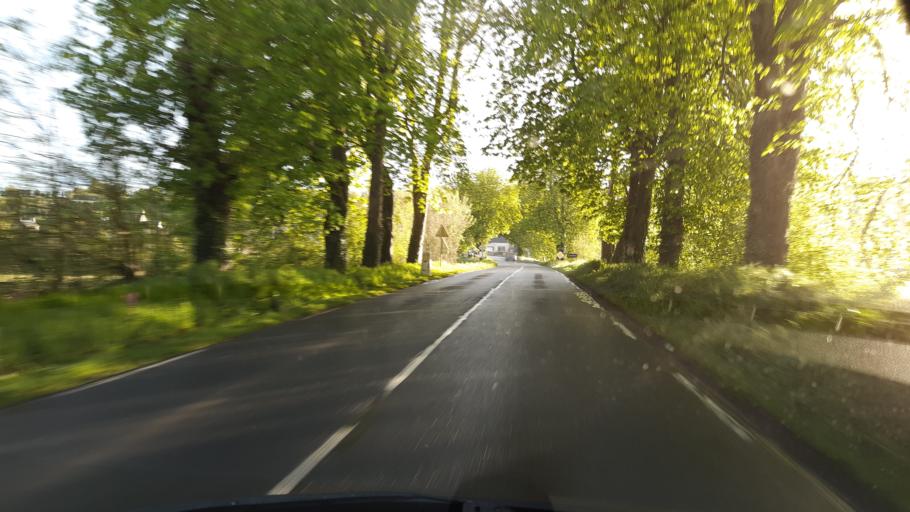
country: FR
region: Lower Normandy
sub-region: Departement de la Manche
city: Agneaux
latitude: 49.0902
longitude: -1.1191
